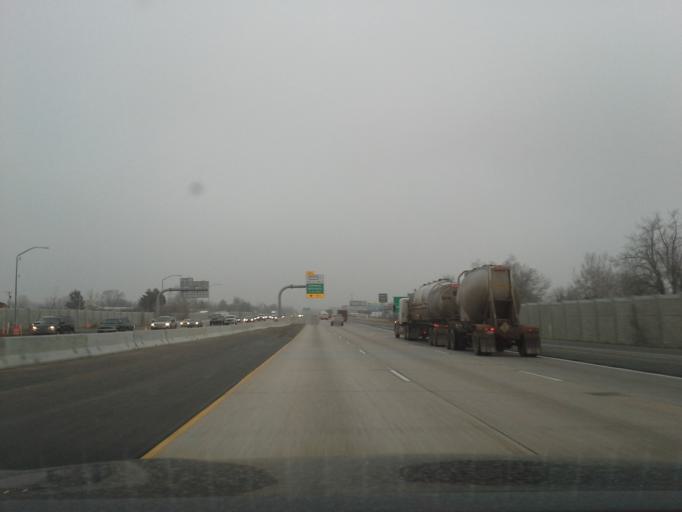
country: US
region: Utah
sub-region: Davis County
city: Layton
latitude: 41.0720
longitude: -111.9751
